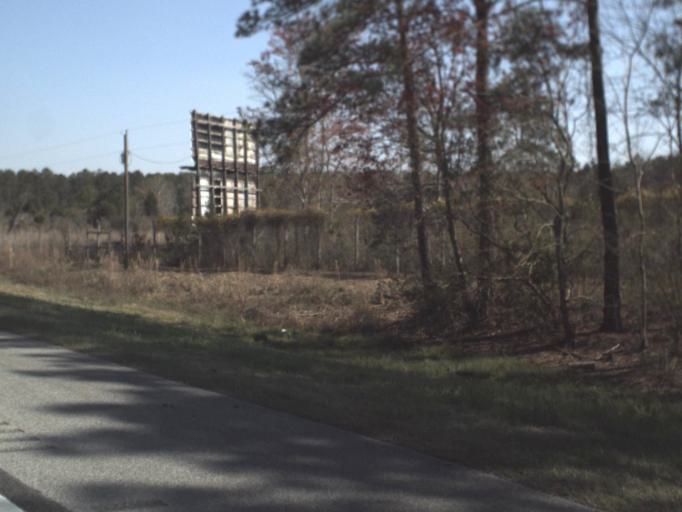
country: US
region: Florida
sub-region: Jackson County
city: Sneads
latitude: 30.6359
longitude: -84.9363
